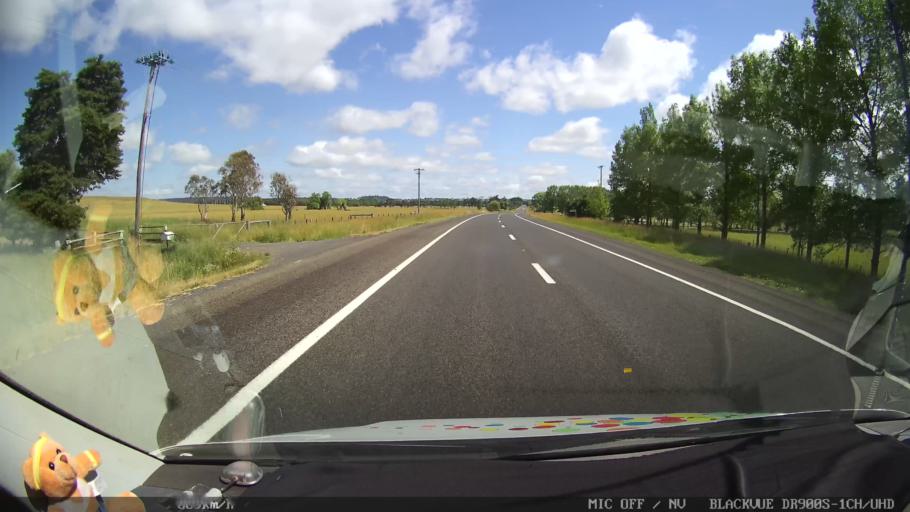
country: AU
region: New South Wales
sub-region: Glen Innes Severn
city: Glen Innes
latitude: -29.8337
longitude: 151.7376
